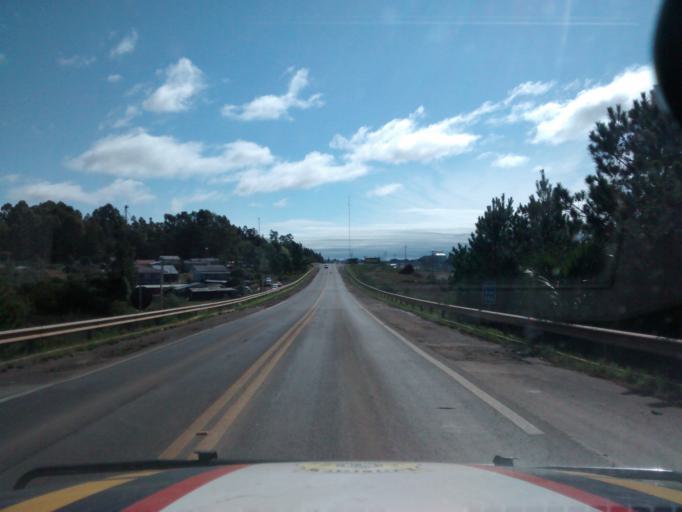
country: BR
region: Rio Grande do Sul
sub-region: Lagoa Vermelha
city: Lagoa Vermelha
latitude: -28.2244
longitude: -51.5078
